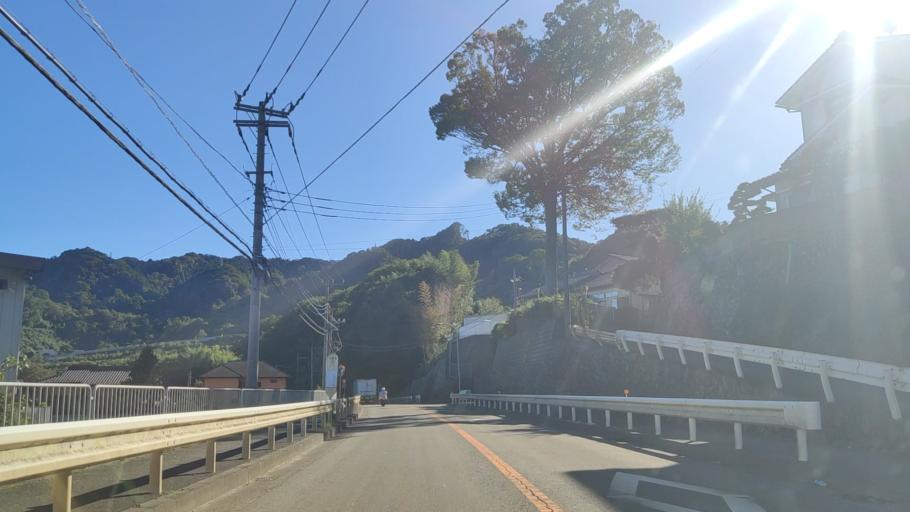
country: JP
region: Tokyo
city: Hachioji
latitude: 35.5824
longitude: 139.2981
